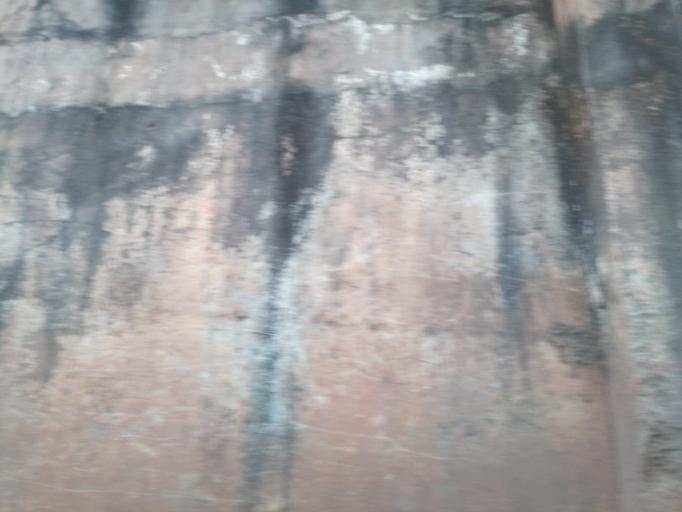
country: TZ
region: Dar es Salaam
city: Magomeni
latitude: -6.7734
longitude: 39.2740
